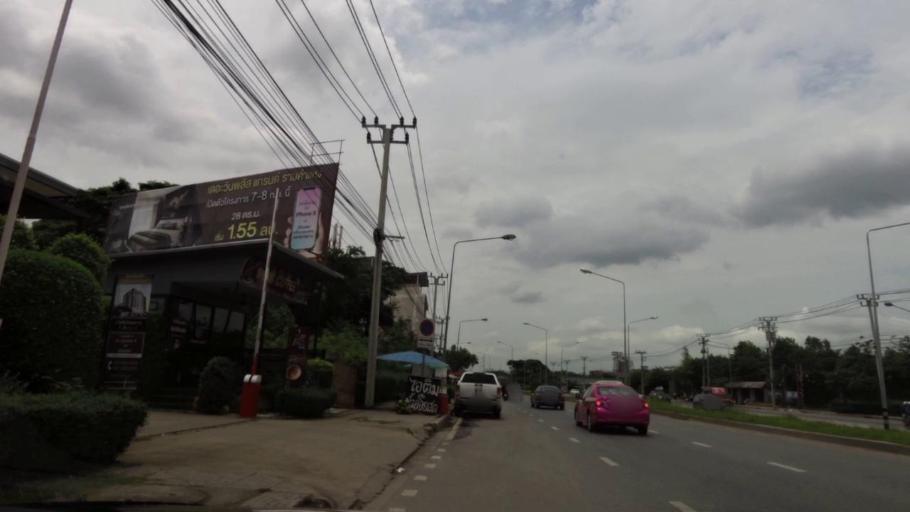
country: TH
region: Bangkok
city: Bang Kapi
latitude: 13.7522
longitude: 100.6368
